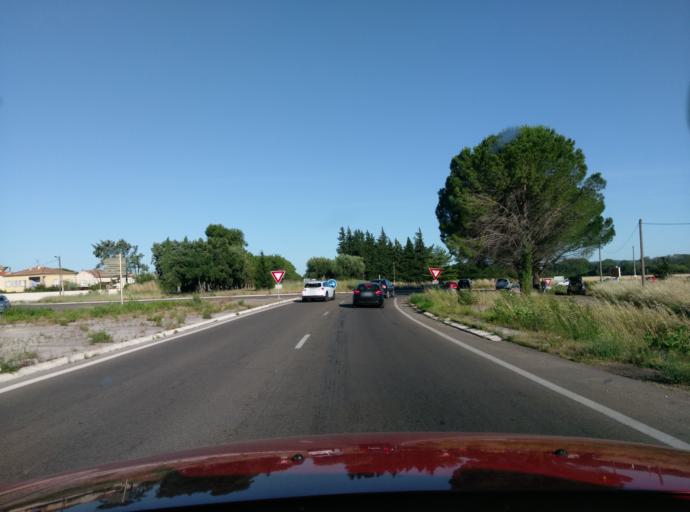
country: FR
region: Languedoc-Roussillon
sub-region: Departement du Gard
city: Rodilhan
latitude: 43.8318
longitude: 4.4417
